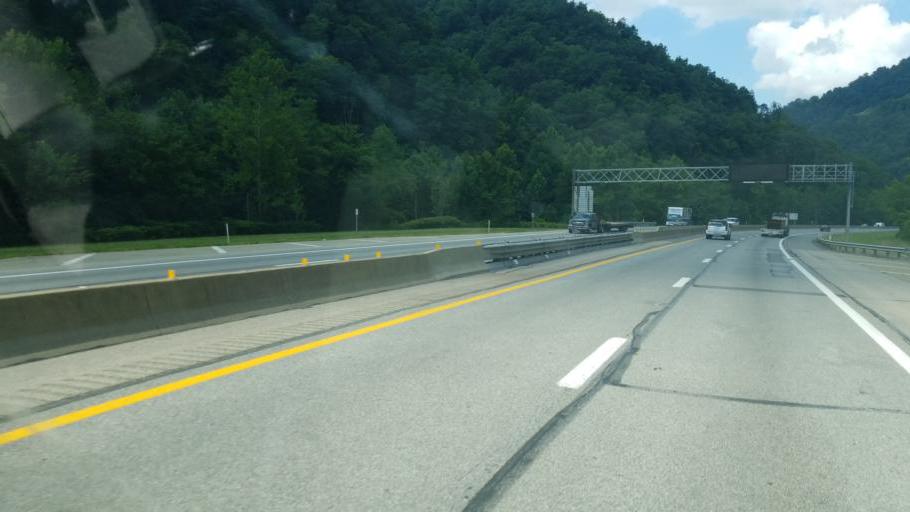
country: US
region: West Virginia
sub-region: Kanawha County
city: Montgomery
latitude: 38.0562
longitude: -81.3758
